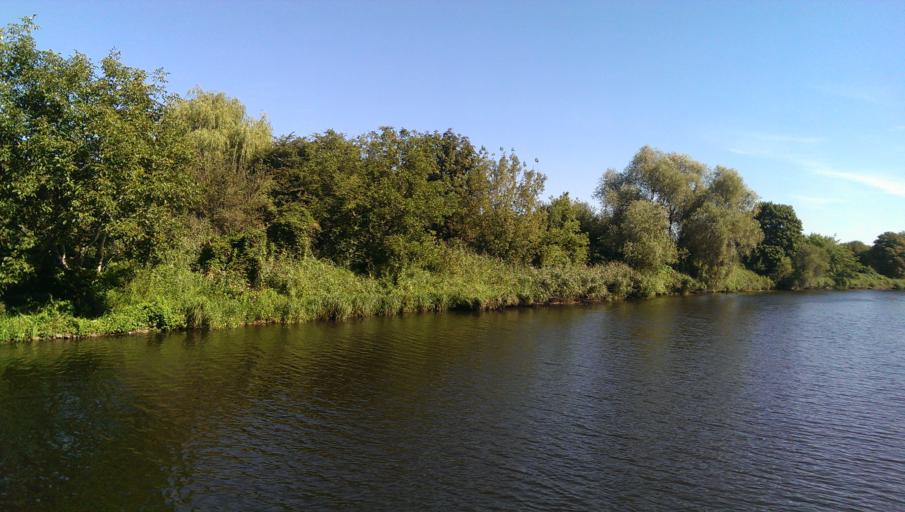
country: DE
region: Brandenburg
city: Teltow
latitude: 52.4064
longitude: 13.2565
